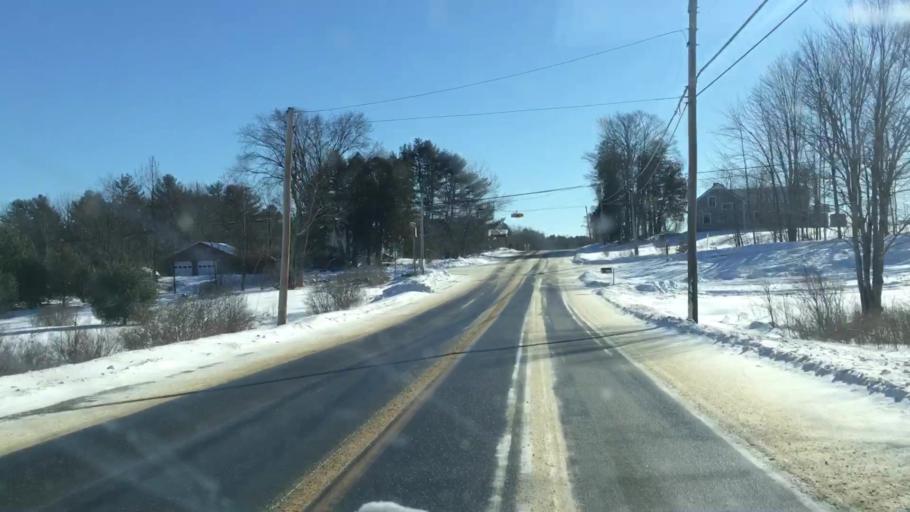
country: US
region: Maine
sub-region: Androscoggin County
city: Lisbon Falls
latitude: 43.9361
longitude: -70.0615
